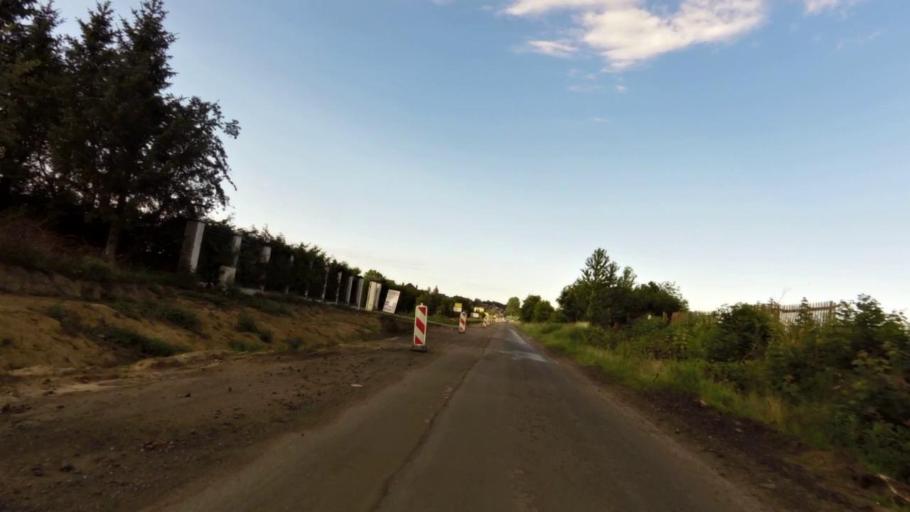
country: PL
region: West Pomeranian Voivodeship
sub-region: Powiat slawienski
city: Darlowo
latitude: 54.4108
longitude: 16.3949
